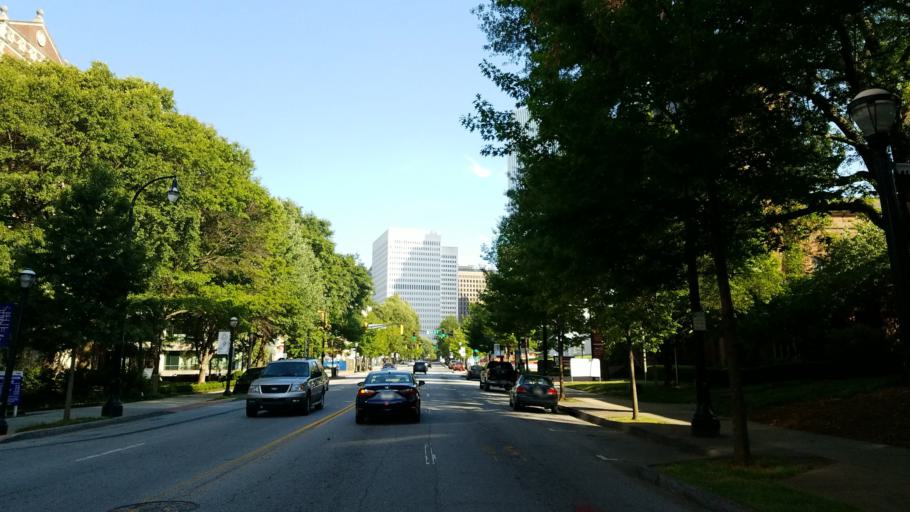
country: US
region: Georgia
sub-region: Fulton County
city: Atlanta
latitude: 33.7914
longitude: -84.3857
